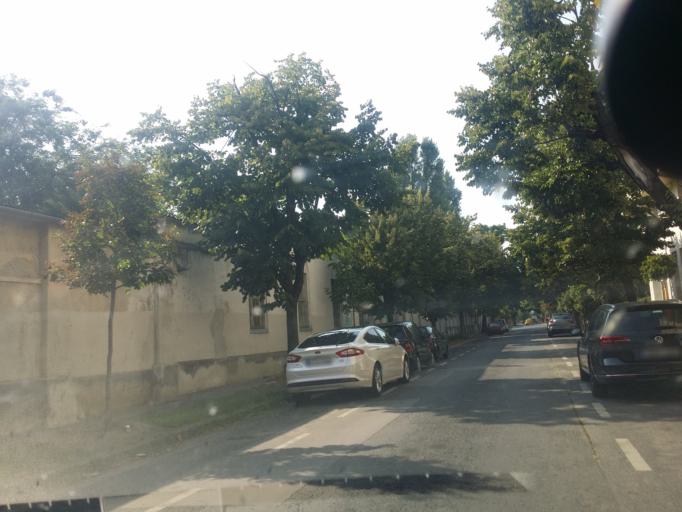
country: HU
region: Budapest
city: Budapest XIII. keruelet
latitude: 47.5306
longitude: 19.0753
